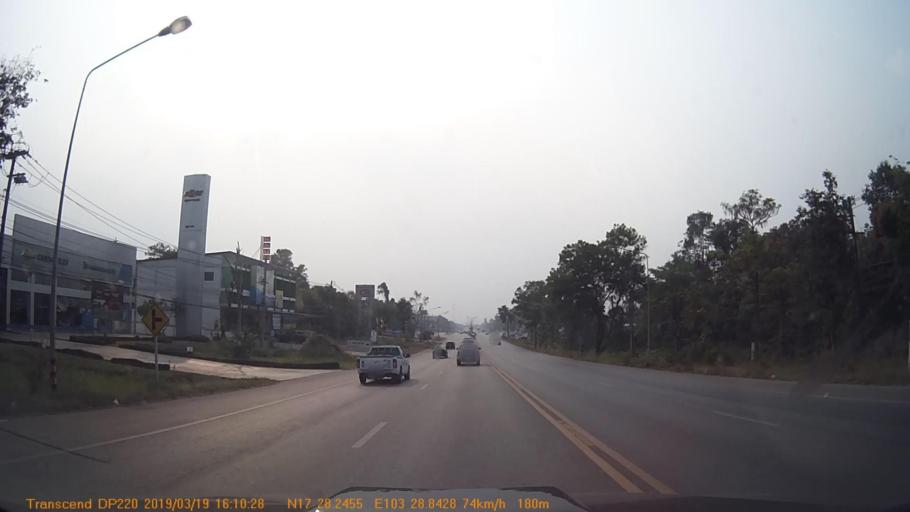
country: TH
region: Sakon Nakhon
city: Sawang Daen Din
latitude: 17.4708
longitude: 103.4804
